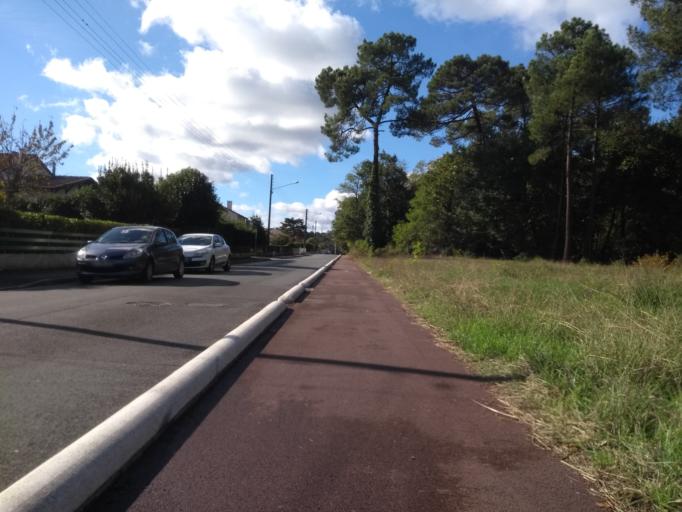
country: FR
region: Aquitaine
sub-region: Departement de la Gironde
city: Pessac
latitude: 44.8135
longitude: -0.6665
